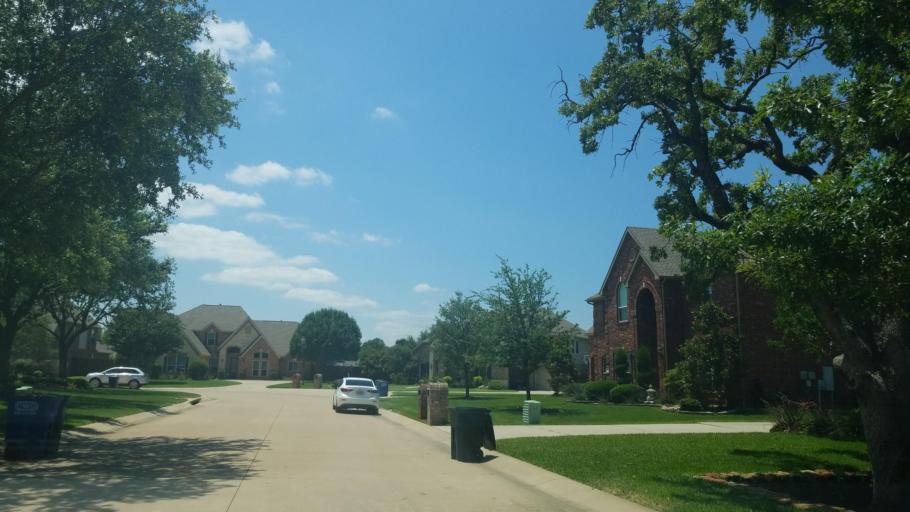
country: US
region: Texas
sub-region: Denton County
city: Copper Canyon
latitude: 33.0795
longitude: -97.0831
